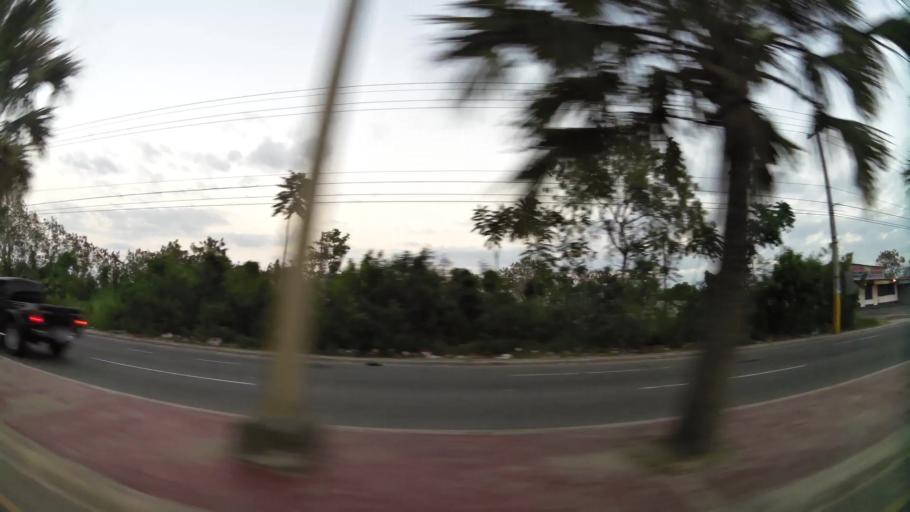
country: DO
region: Nacional
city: La Agustina
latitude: 18.5416
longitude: -69.9539
